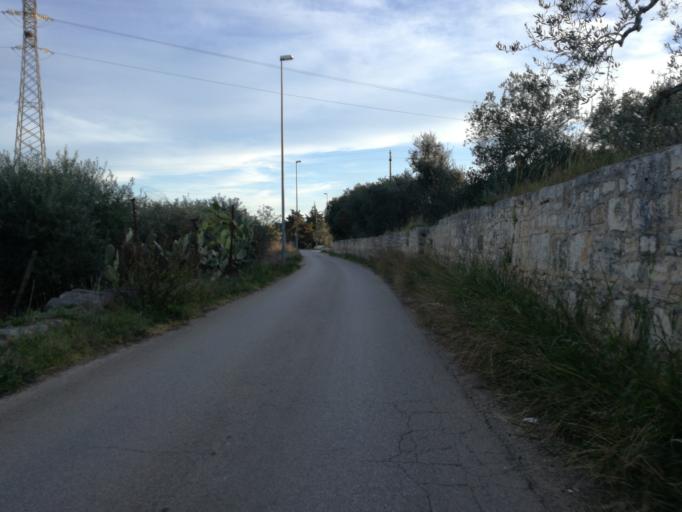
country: IT
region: Apulia
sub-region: Provincia di Bari
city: Lamie
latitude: 41.0365
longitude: 16.8808
